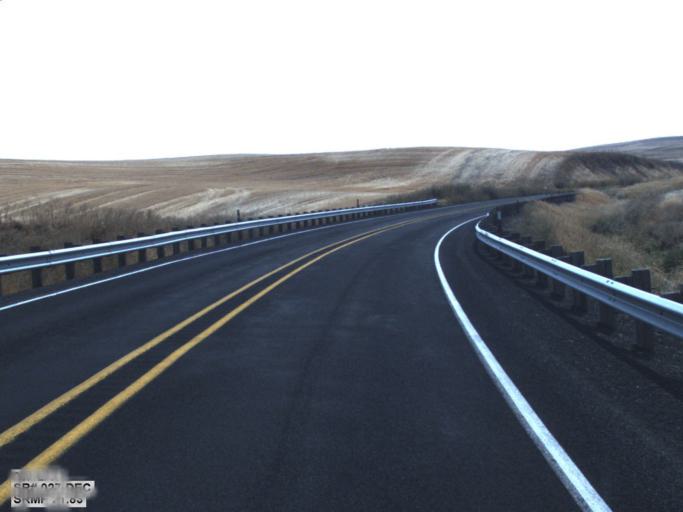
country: US
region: Washington
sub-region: Whitman County
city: Pullman
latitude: 46.9801
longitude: -117.1220
